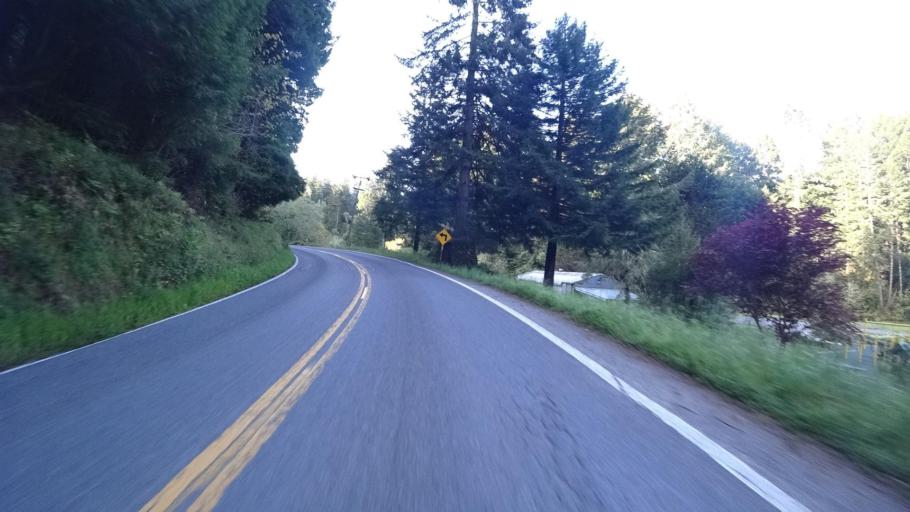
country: US
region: California
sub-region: Humboldt County
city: Myrtletown
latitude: 40.7561
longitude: -124.0492
